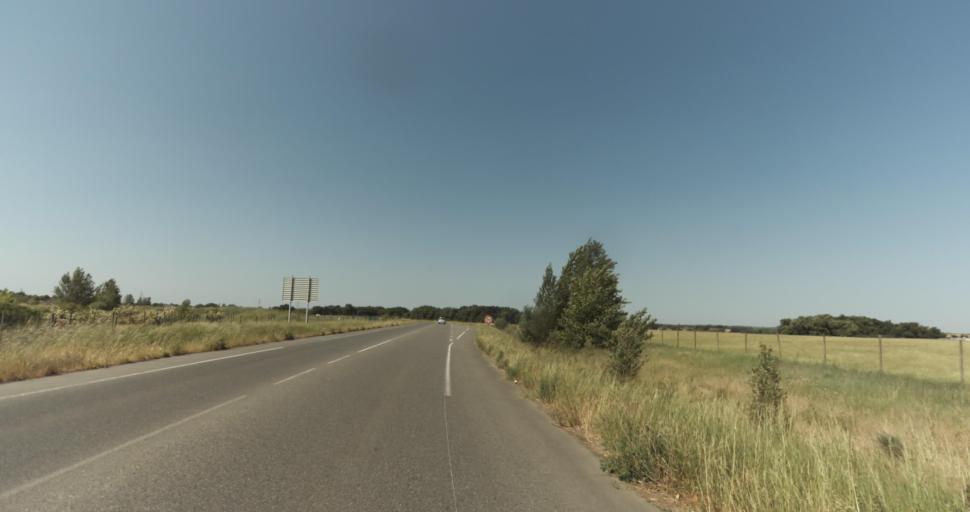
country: FR
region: Midi-Pyrenees
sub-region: Departement de la Haute-Garonne
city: La Salvetat-Saint-Gilles
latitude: 43.5907
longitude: 1.2838
